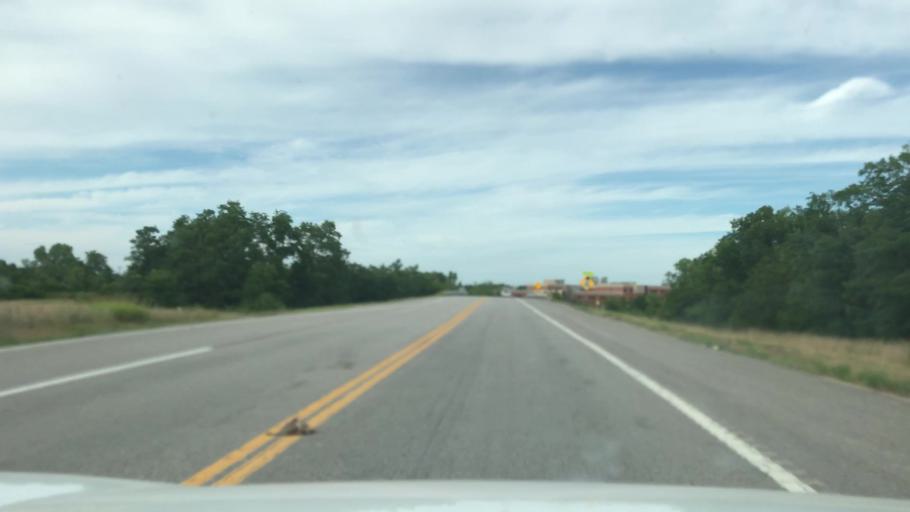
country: US
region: Missouri
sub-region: Saint Charles County
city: Weldon Spring
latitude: 38.6982
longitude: -90.7214
